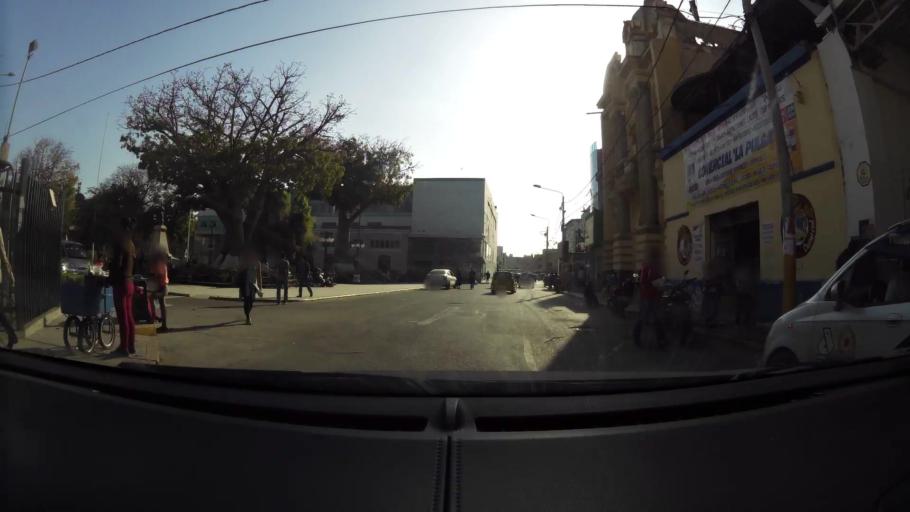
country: PE
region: Lambayeque
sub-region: Provincia de Chiclayo
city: Chiclayo
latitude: -6.7708
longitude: -79.8428
